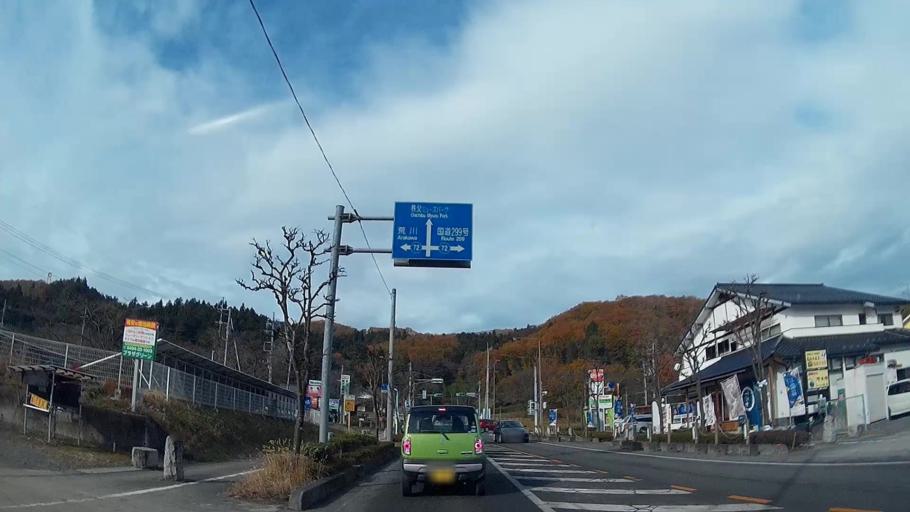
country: JP
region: Saitama
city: Chichibu
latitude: 36.0035
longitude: 139.0690
